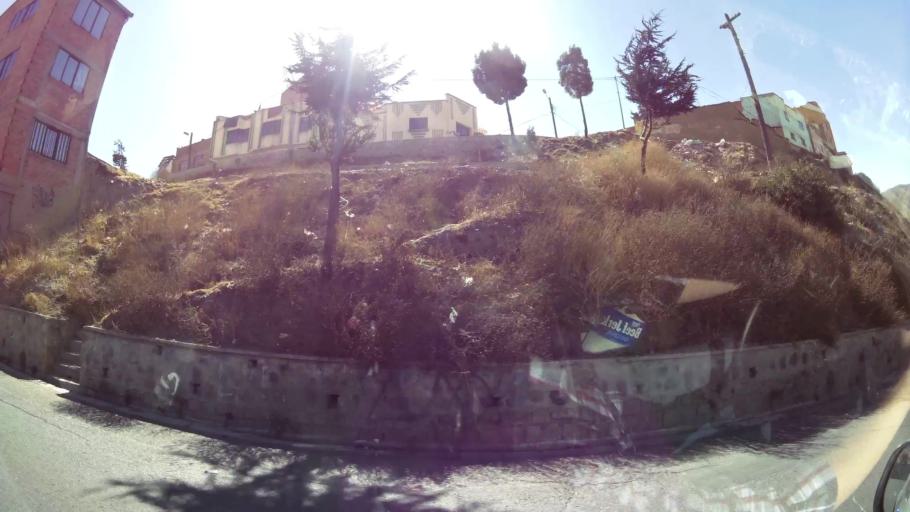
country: BO
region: La Paz
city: La Paz
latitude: -16.4925
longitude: -68.1480
